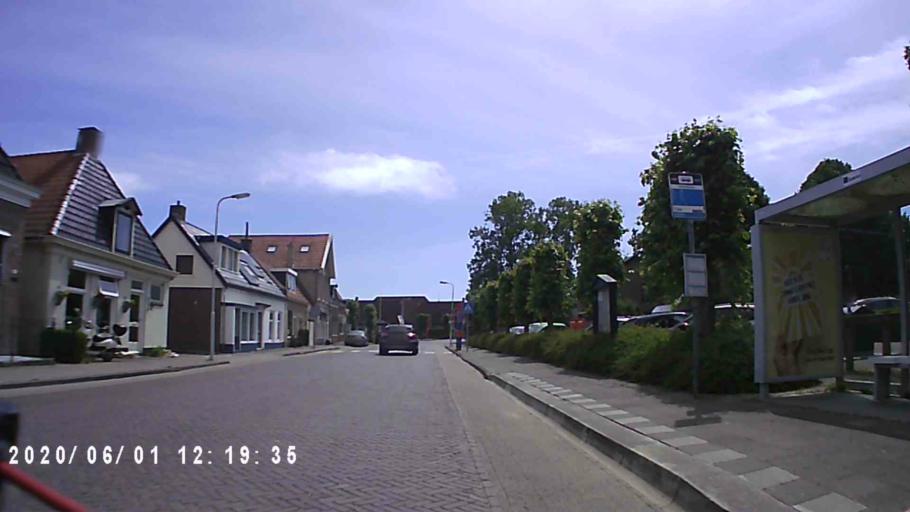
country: NL
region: Friesland
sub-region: Gemeente Harlingen
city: Harlingen
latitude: 53.1302
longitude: 5.4756
